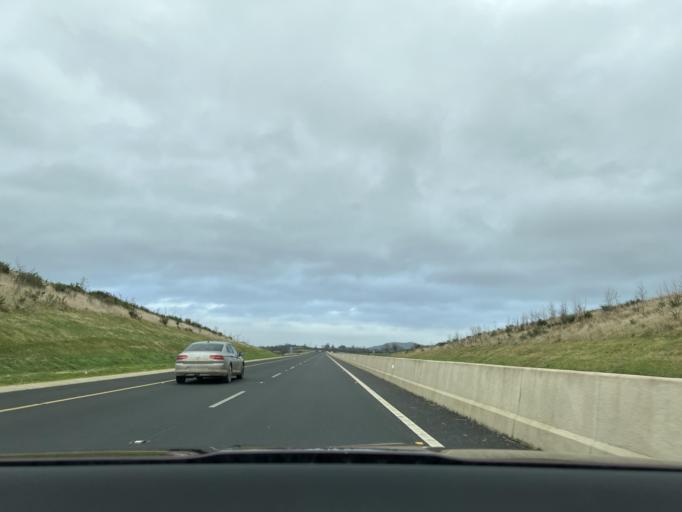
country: IE
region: Leinster
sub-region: Loch Garman
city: Ferns
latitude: 52.5565
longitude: -6.4750
